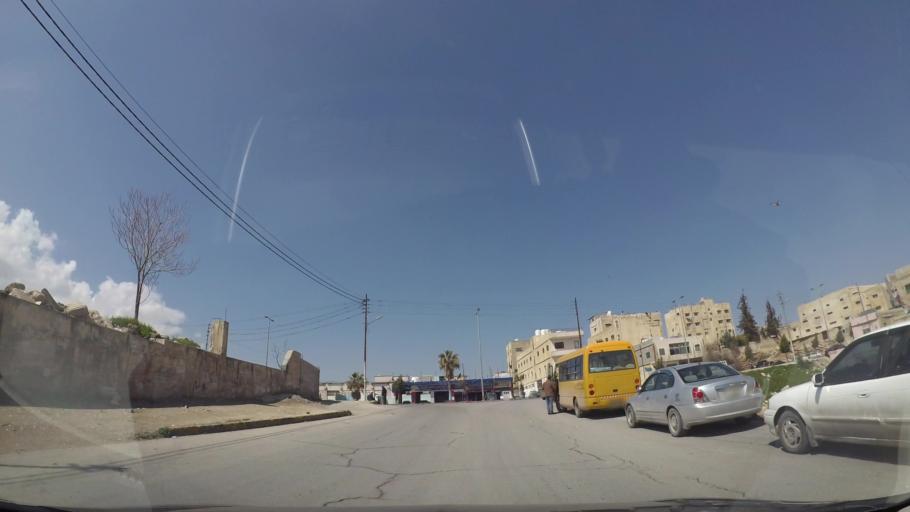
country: JO
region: Zarqa
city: Russeifa
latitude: 31.9861
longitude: 35.9988
